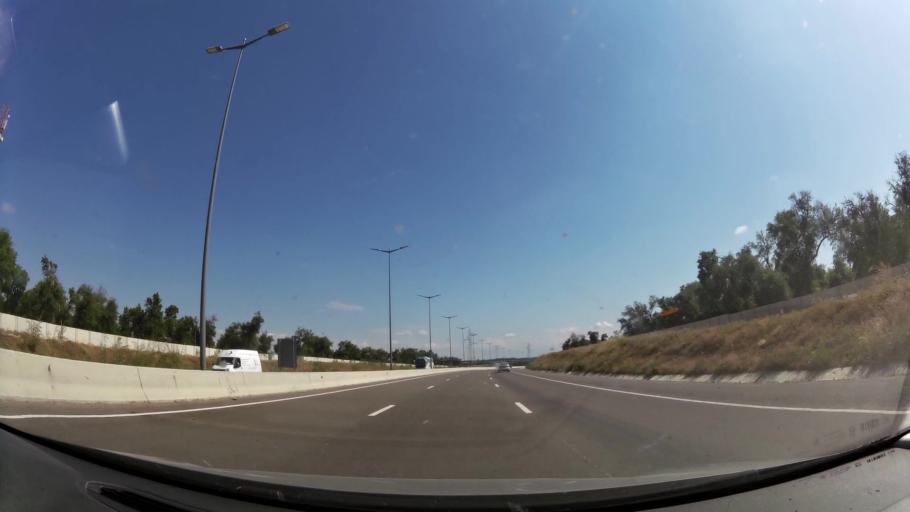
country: MA
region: Rabat-Sale-Zemmour-Zaer
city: Sale
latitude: 34.0158
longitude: -6.7085
